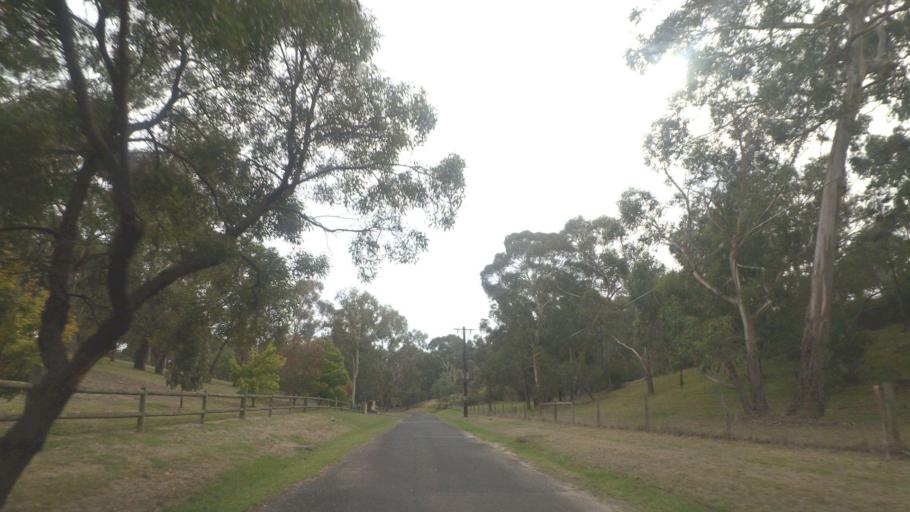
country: AU
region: Victoria
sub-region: Manningham
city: Park Orchards
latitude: -37.7694
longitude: 145.1948
